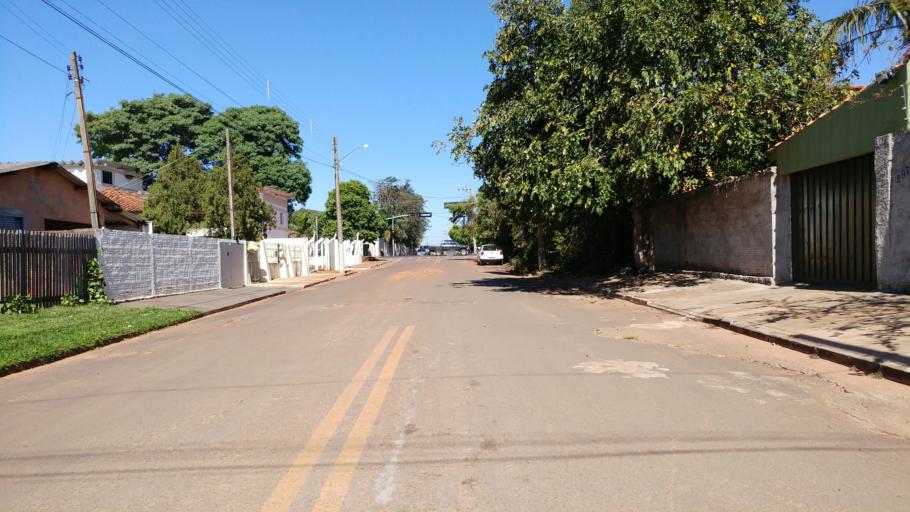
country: BR
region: Sao Paulo
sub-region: Paraguacu Paulista
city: Paraguacu Paulista
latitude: -22.4296
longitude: -50.5862
